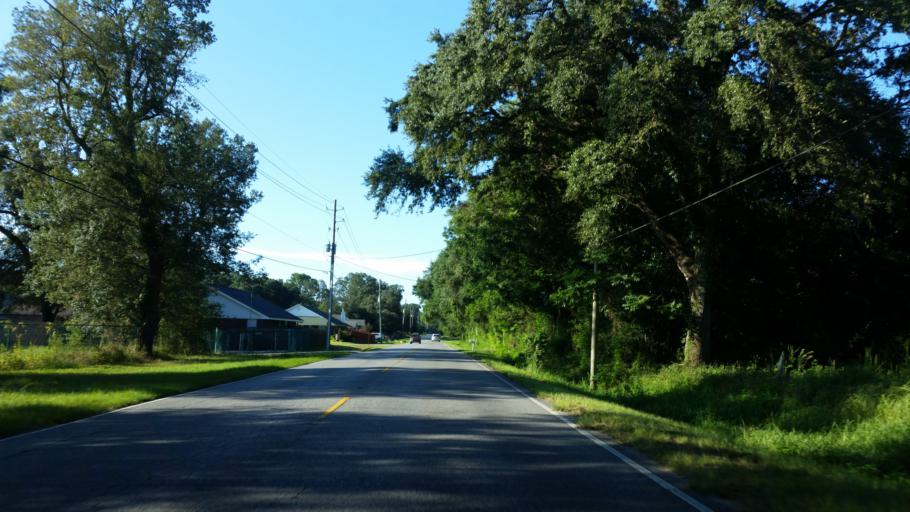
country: US
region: Florida
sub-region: Escambia County
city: Bellview
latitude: 30.4581
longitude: -87.3160
